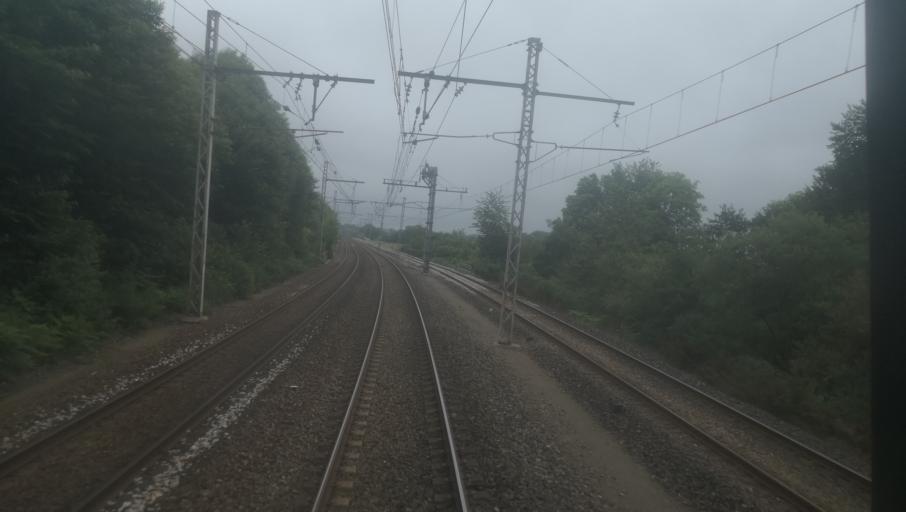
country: FR
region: Limousin
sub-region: Departement de la Creuse
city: Saint-Agnant-de-Versillat
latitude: 46.3160
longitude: 1.5231
